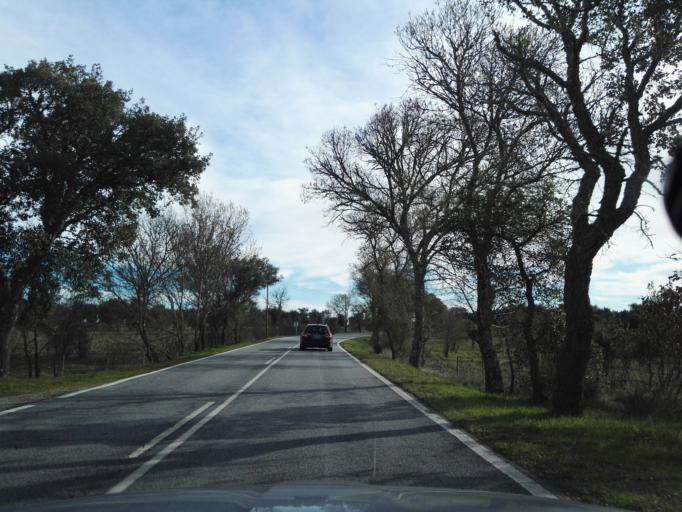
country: PT
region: Portalegre
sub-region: Nisa
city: Nisa
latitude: 39.5000
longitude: -7.6884
